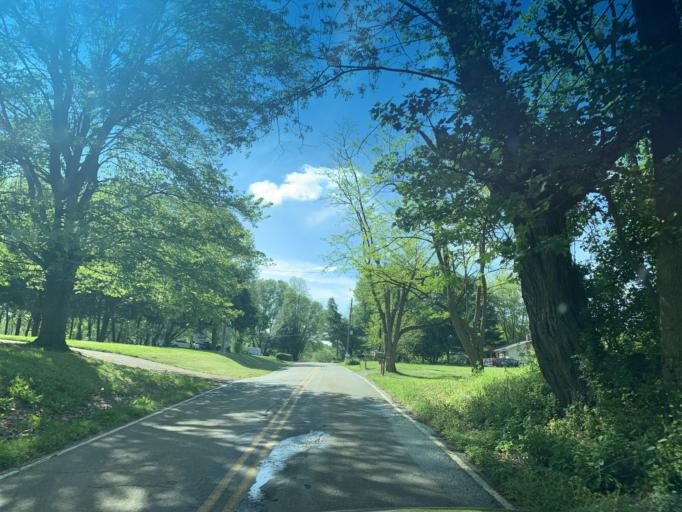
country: US
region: Maryland
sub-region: Cecil County
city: Rising Sun
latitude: 39.6935
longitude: -76.1508
